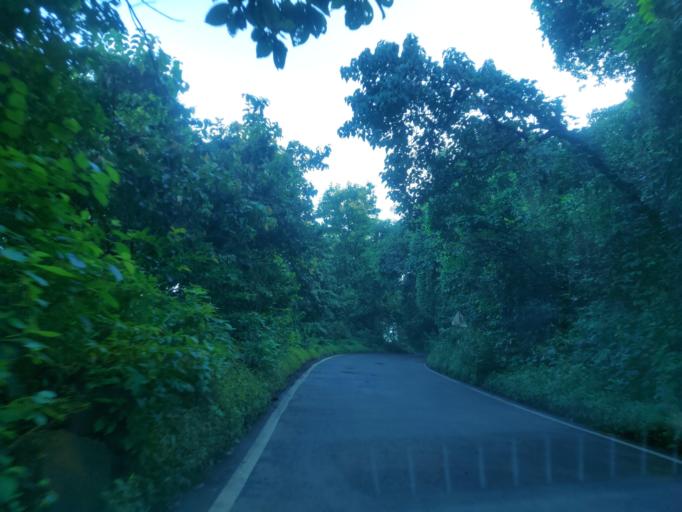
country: IN
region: Maharashtra
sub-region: Sindhudurg
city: Savantvadi
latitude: 15.9372
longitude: 73.9477
